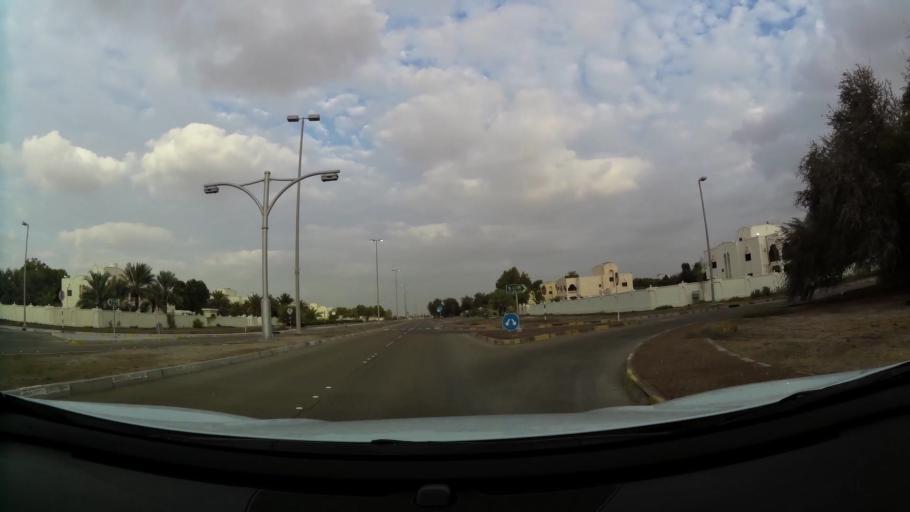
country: AE
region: Abu Dhabi
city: Abu Dhabi
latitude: 24.3828
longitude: 54.5290
